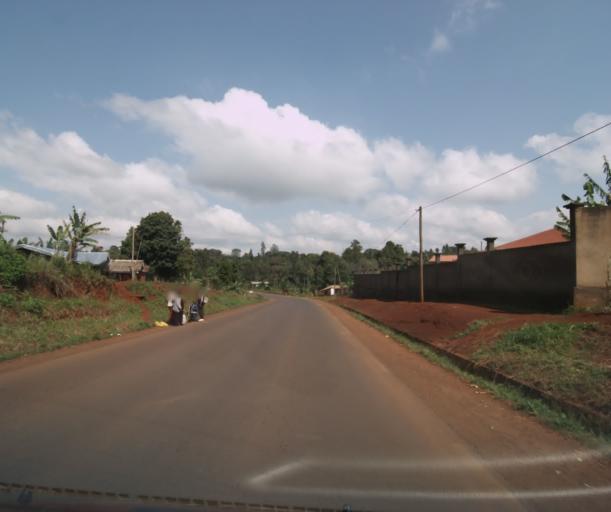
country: CM
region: West
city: Bansoa
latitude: 5.4912
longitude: 10.1885
